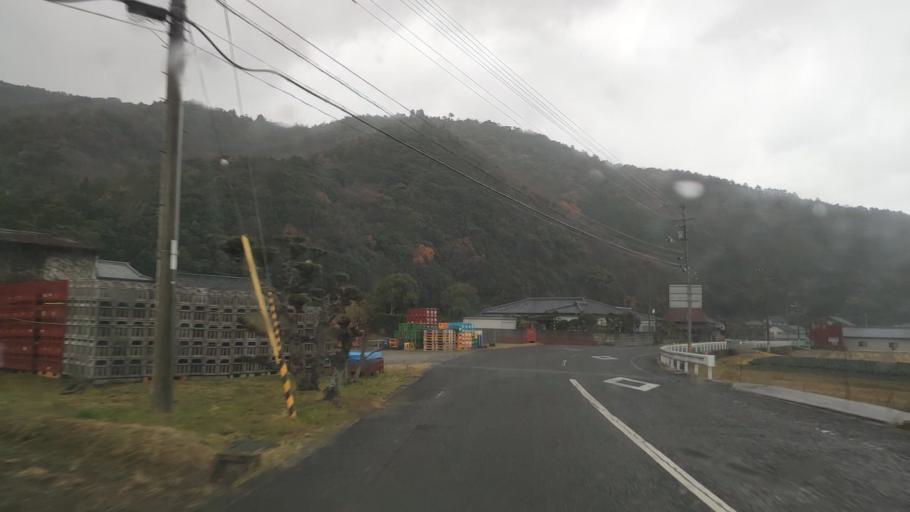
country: JP
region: Tokushima
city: Ishii
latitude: 34.1964
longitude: 134.4005
